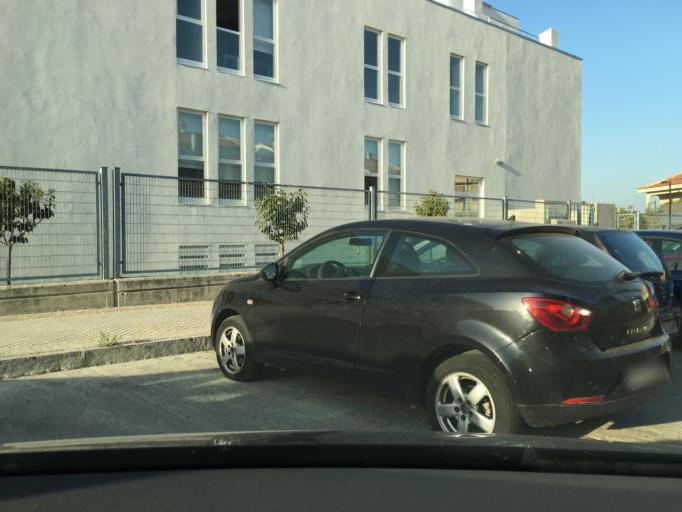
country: ES
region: Andalusia
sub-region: Provincia de Granada
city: Maracena
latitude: 37.1983
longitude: -3.6239
